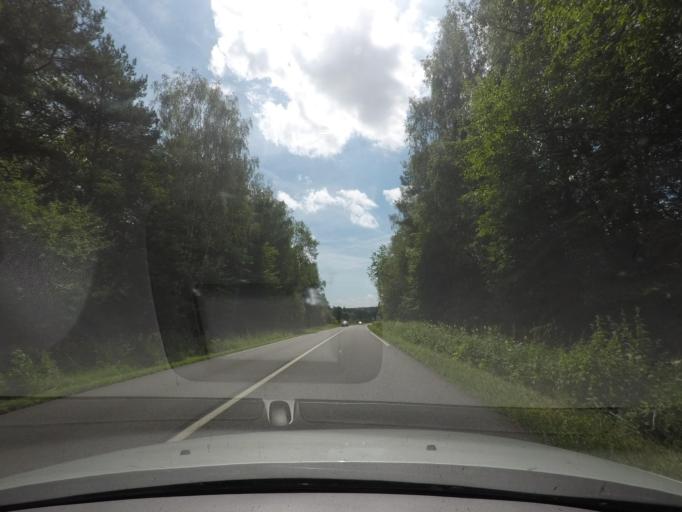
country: FR
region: Alsace
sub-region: Departement du Bas-Rhin
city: Drulingen
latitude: 48.8679
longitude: 7.1755
